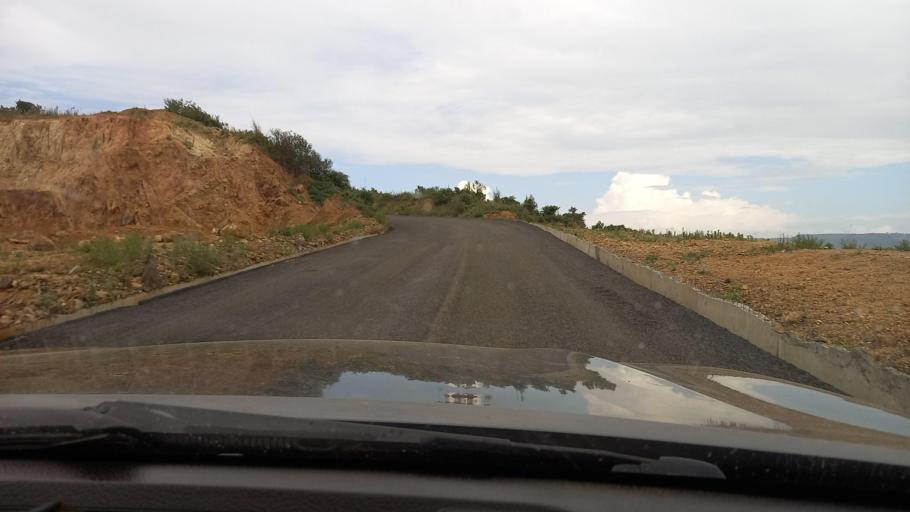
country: ET
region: Southern Nations, Nationalities, and People's Region
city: Mizan Teferi
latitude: 6.2077
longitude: 35.6553
